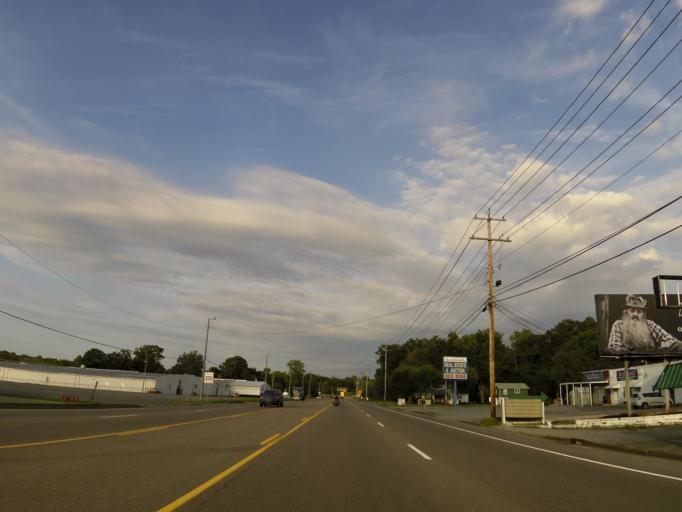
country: US
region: Tennessee
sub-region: Cocke County
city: Newport
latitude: 35.9747
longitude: -83.2254
